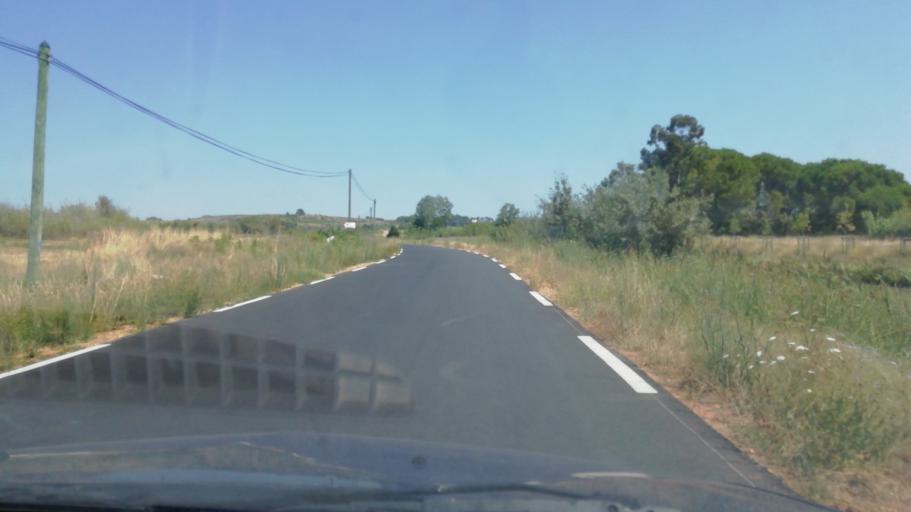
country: FR
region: Languedoc-Roussillon
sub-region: Departement de l'Herault
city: Capestang
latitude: 43.3305
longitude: 3.0512
